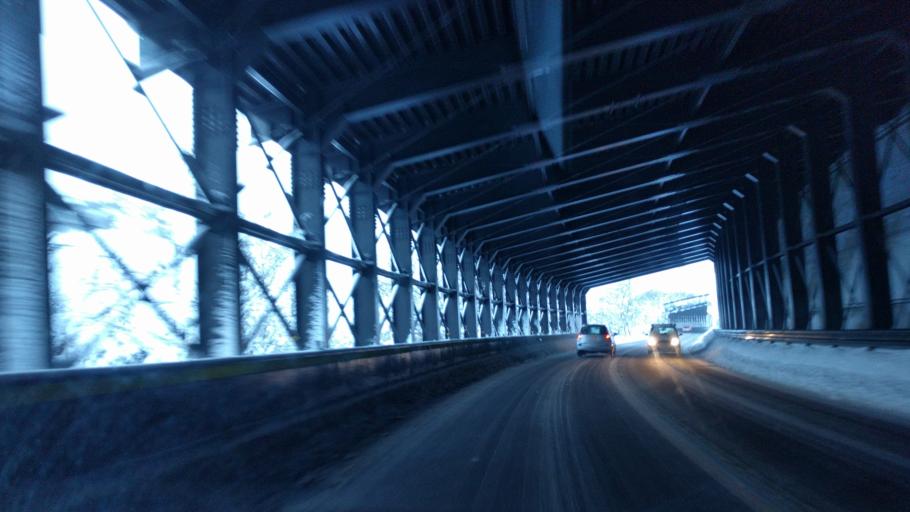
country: JP
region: Fukushima
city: Inawashiro
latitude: 37.5111
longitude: 140.0307
